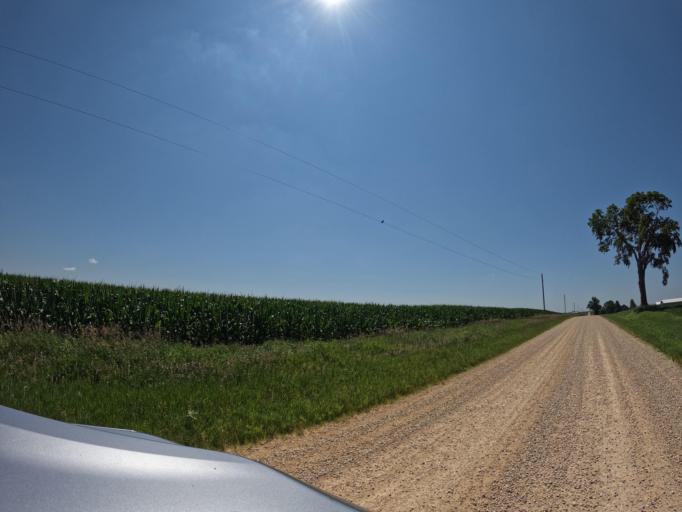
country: US
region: Iowa
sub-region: Clinton County
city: Camanche
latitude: 41.7998
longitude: -90.3937
